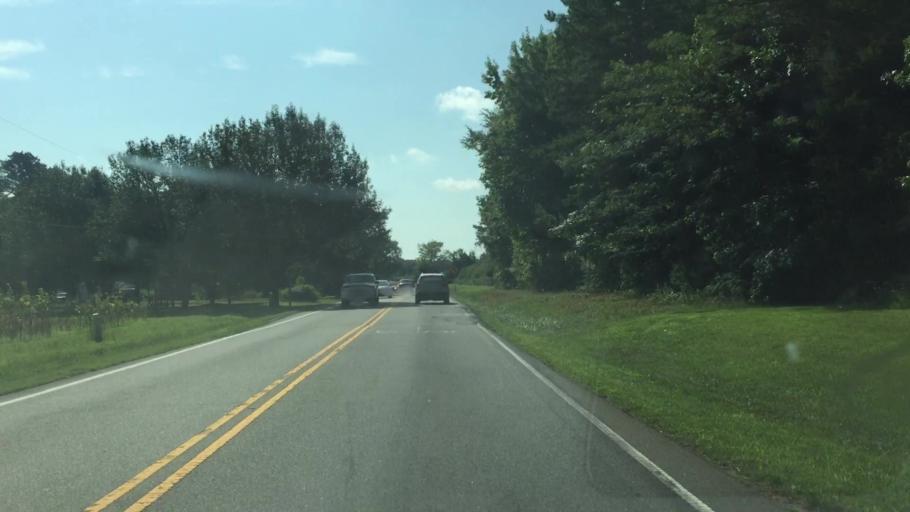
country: US
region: North Carolina
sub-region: Mecklenburg County
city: Mint Hill
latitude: 35.1741
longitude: -80.6205
